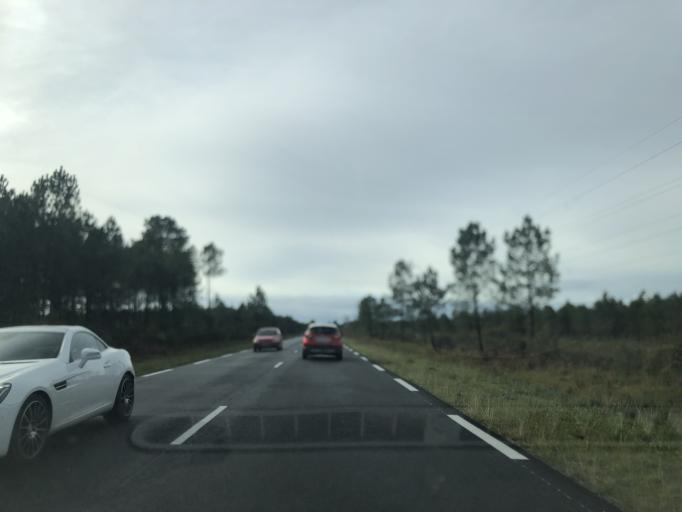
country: FR
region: Aquitaine
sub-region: Departement de la Gironde
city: Martignas-sur-Jalle
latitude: 44.8074
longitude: -0.8623
